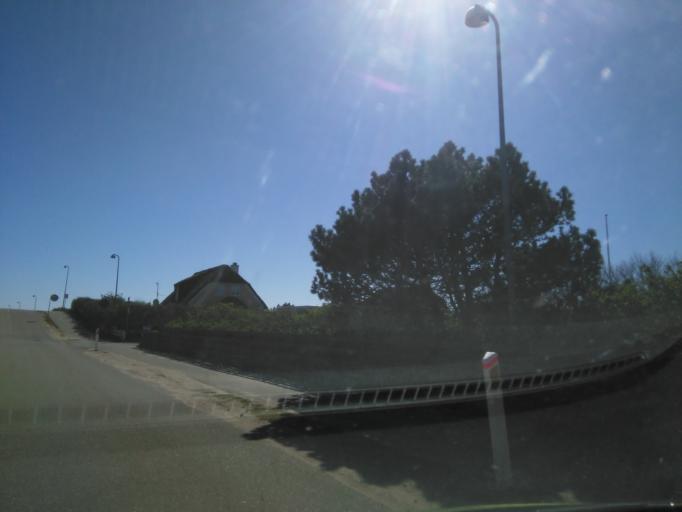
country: DK
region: South Denmark
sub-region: Varde Kommune
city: Oksbol
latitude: 55.5456
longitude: 8.1338
